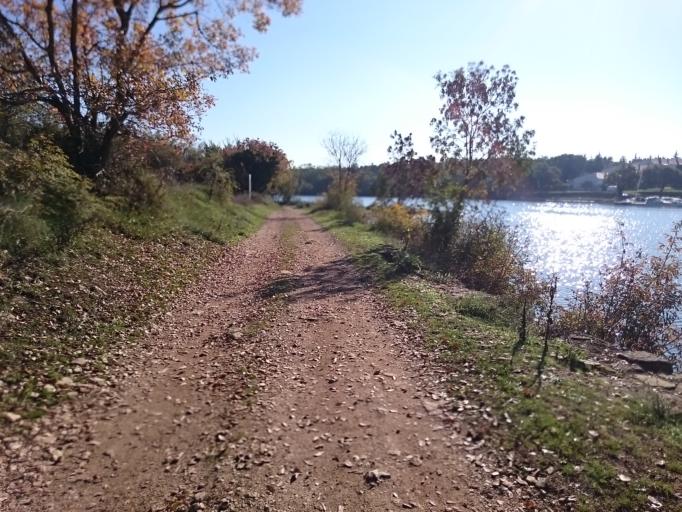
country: HR
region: Istarska
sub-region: Grad Porec
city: Porec
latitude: 45.2780
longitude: 13.5996
